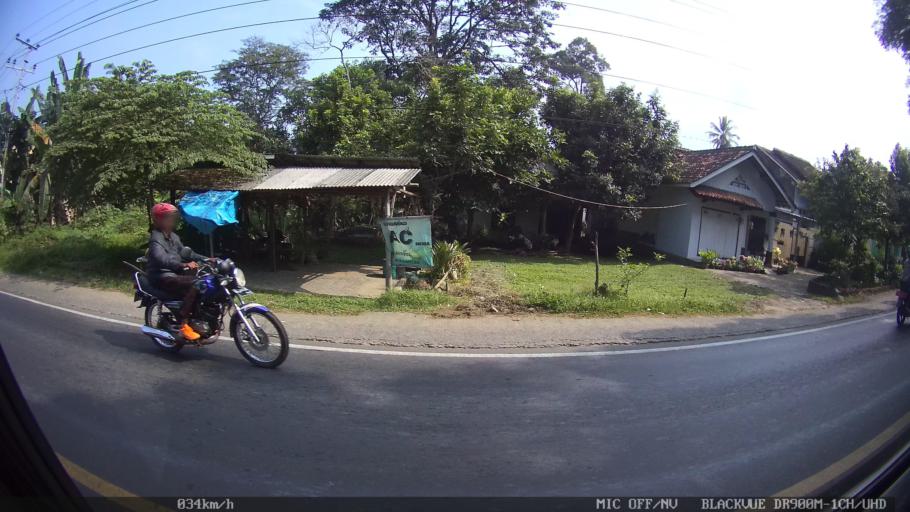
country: ID
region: Lampung
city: Natar
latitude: -5.3696
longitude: 105.1754
